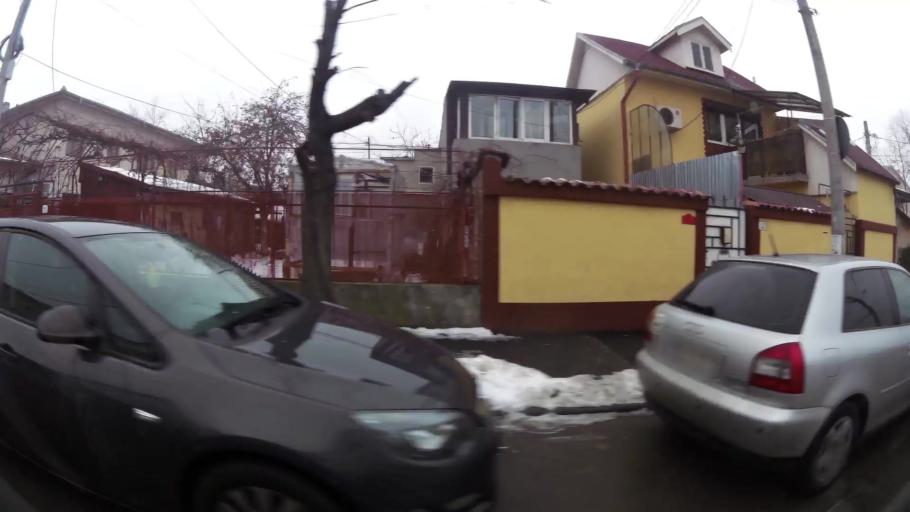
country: RO
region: Ilfov
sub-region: Comuna Chiajna
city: Rosu
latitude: 44.4691
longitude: 26.0324
